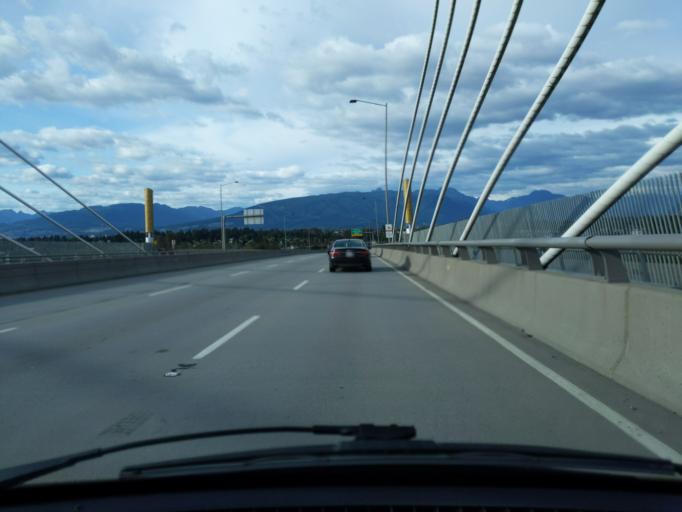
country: CA
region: British Columbia
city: Pitt Meadows
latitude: 49.1994
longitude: -122.6663
